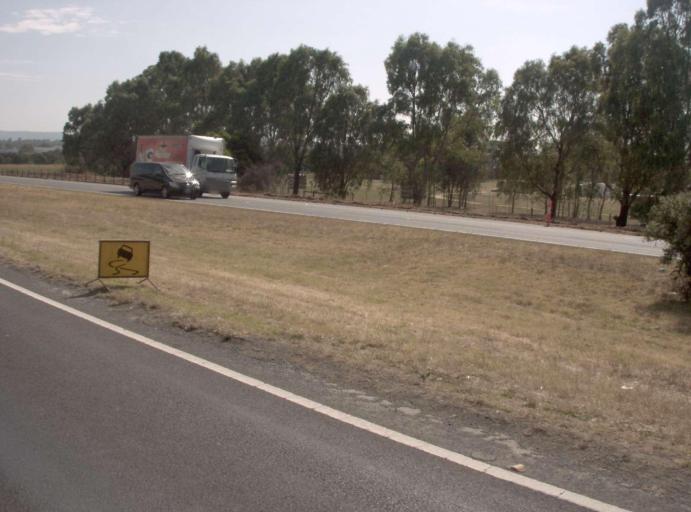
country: AU
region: Victoria
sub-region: Casey
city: Hampton Park
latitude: -38.0202
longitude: 145.2481
